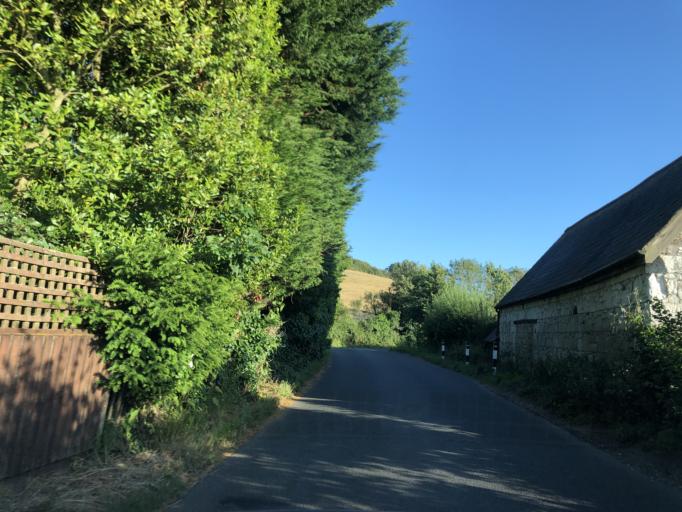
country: GB
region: England
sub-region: Isle of Wight
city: Shalfleet
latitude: 50.6521
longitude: -1.3997
